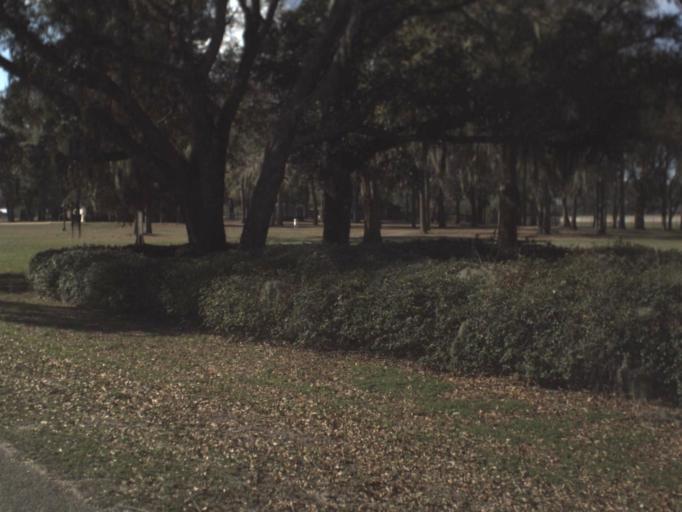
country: US
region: Florida
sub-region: Jackson County
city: Malone
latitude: 30.9686
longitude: -85.1629
